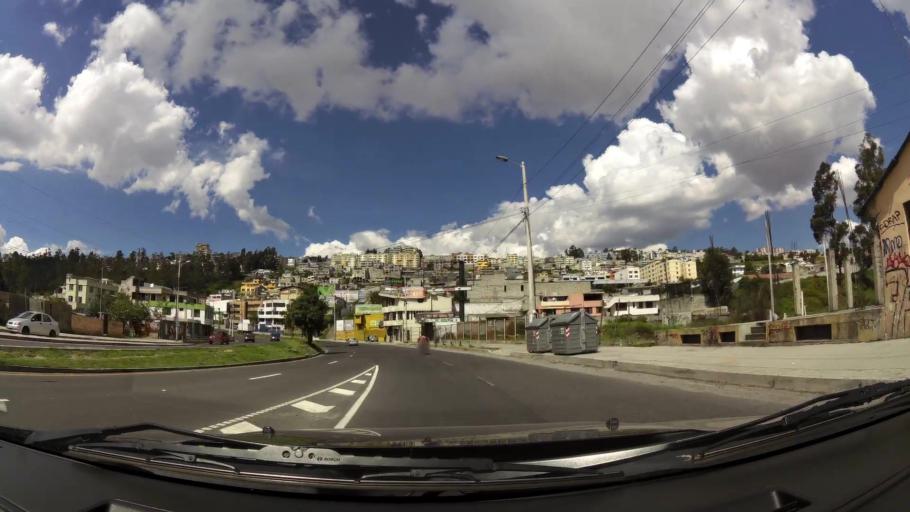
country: EC
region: Pichincha
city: Quito
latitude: -0.1028
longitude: -78.4887
